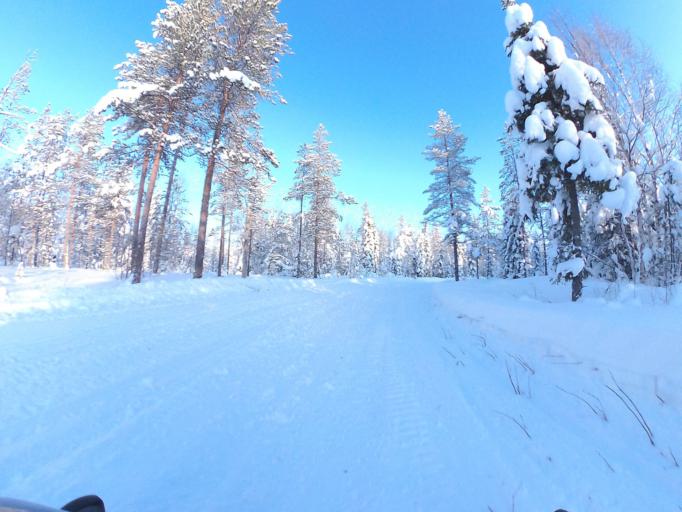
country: FI
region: Lapland
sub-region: Rovaniemi
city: Rovaniemi
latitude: 66.5970
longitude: 25.8518
